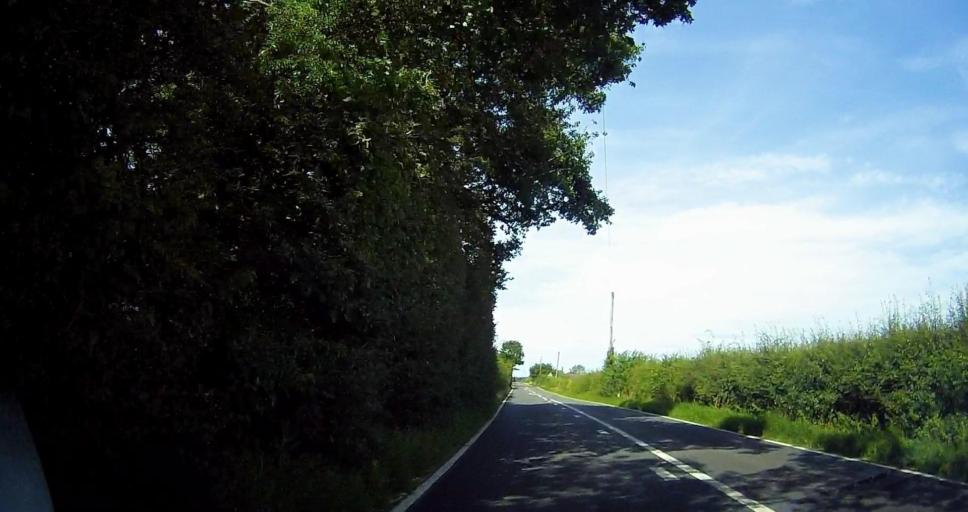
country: GB
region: England
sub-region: Shropshire
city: Market Drayton
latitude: 52.9211
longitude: -2.4965
